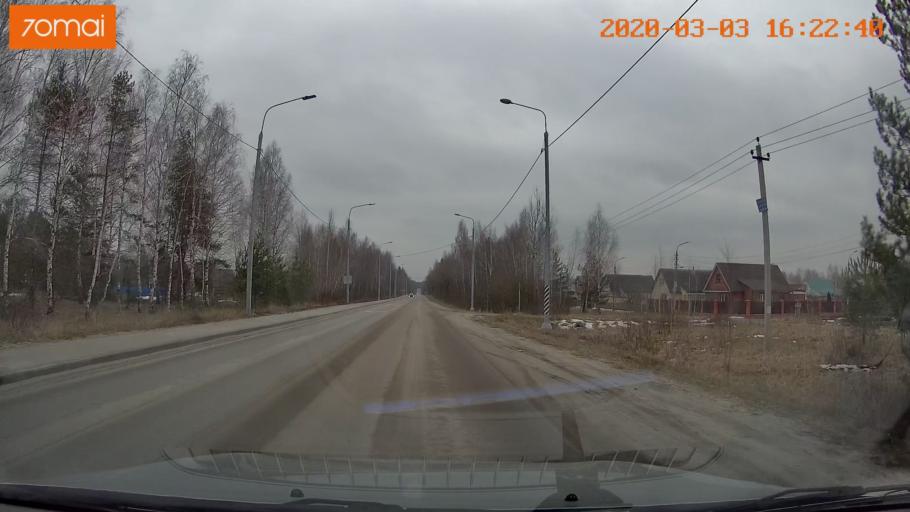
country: RU
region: Moskovskaya
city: Imeni Tsyurupy
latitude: 55.4907
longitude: 38.6486
